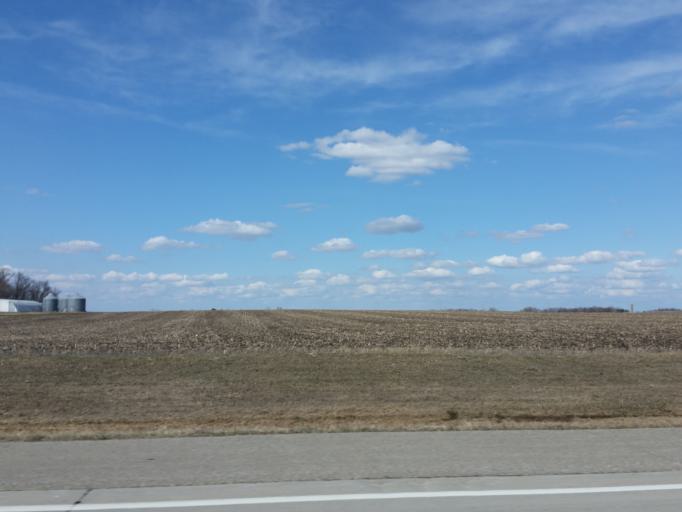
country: US
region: Minnesota
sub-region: Lac qui Parle County
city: Dawson
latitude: 44.9357
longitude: -96.1159
